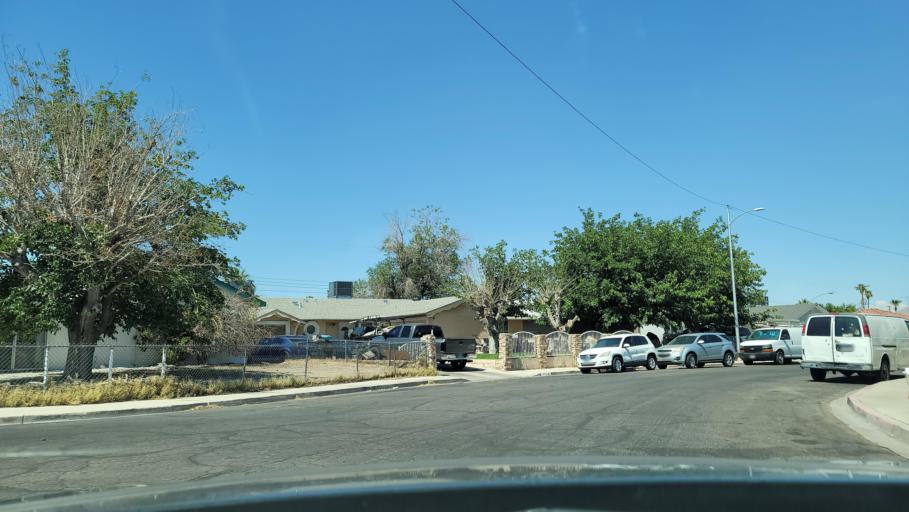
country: US
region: Nevada
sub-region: Clark County
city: Las Vegas
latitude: 36.1837
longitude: -115.1235
